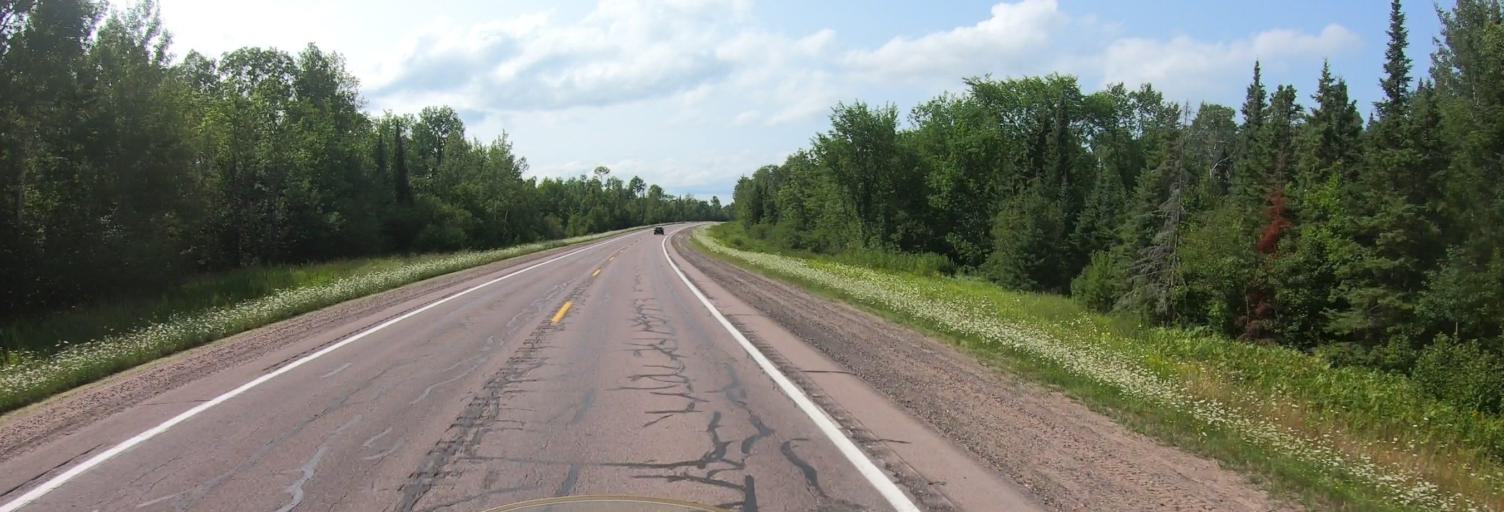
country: US
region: Michigan
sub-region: Ontonagon County
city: Ontonagon
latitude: 46.5804
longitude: -89.5107
